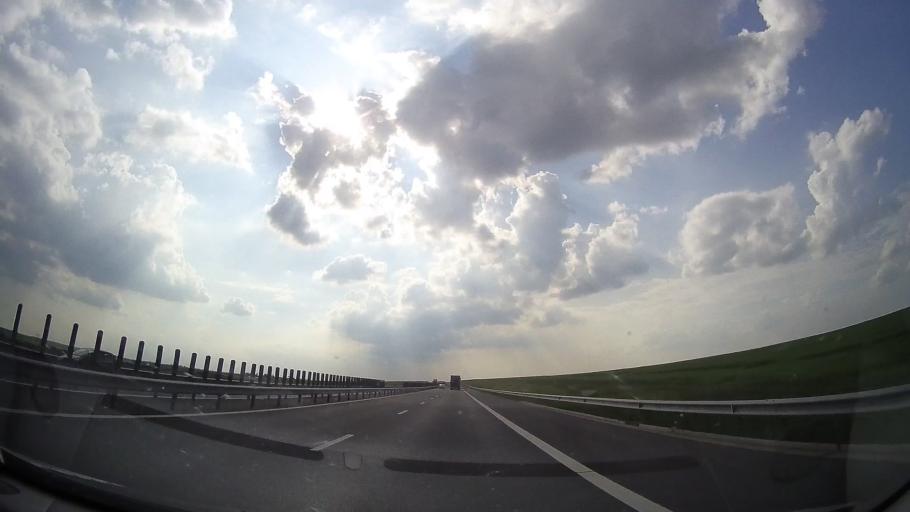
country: RO
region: Timis
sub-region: Oras Recas
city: Recas
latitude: 45.8109
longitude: 21.5496
